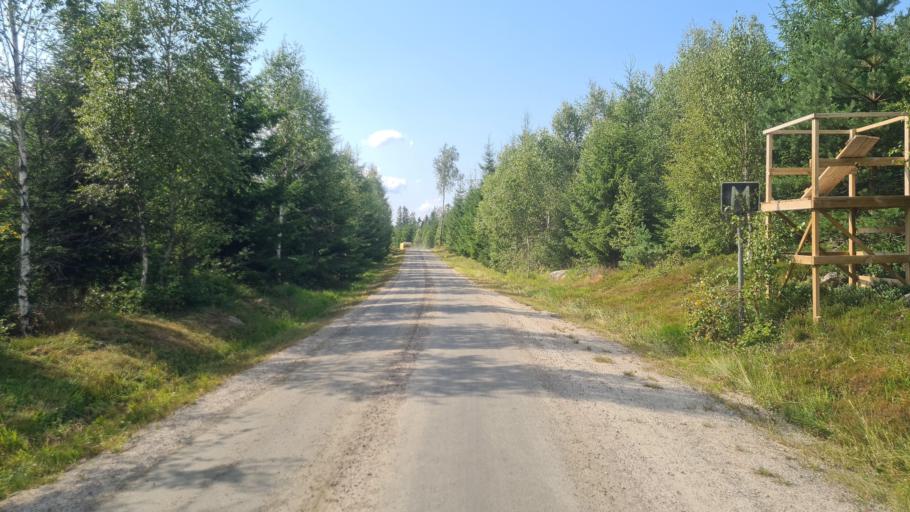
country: SE
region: Kronoberg
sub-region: Ljungby Kommun
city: Ljungby
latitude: 56.7277
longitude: 13.8820
